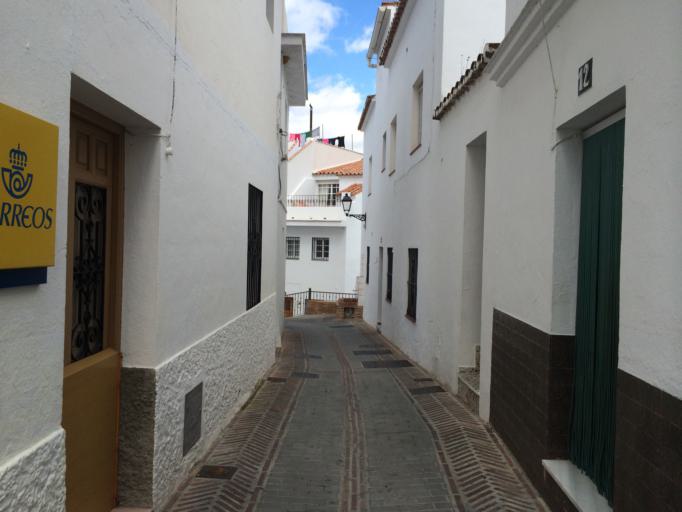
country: ES
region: Andalusia
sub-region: Provincia de Malaga
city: Istan
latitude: 36.5825
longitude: -4.9497
